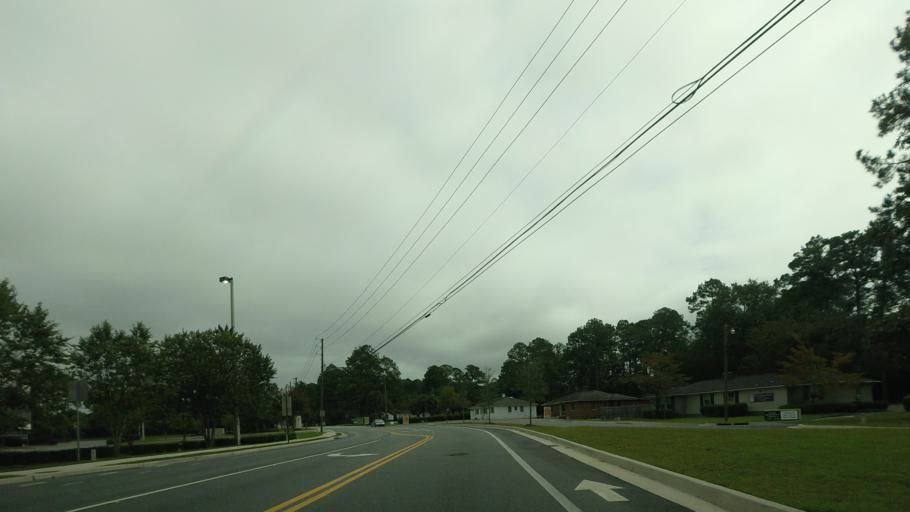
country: US
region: Georgia
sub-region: Lowndes County
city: Remerton
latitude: 30.8595
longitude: -83.2885
